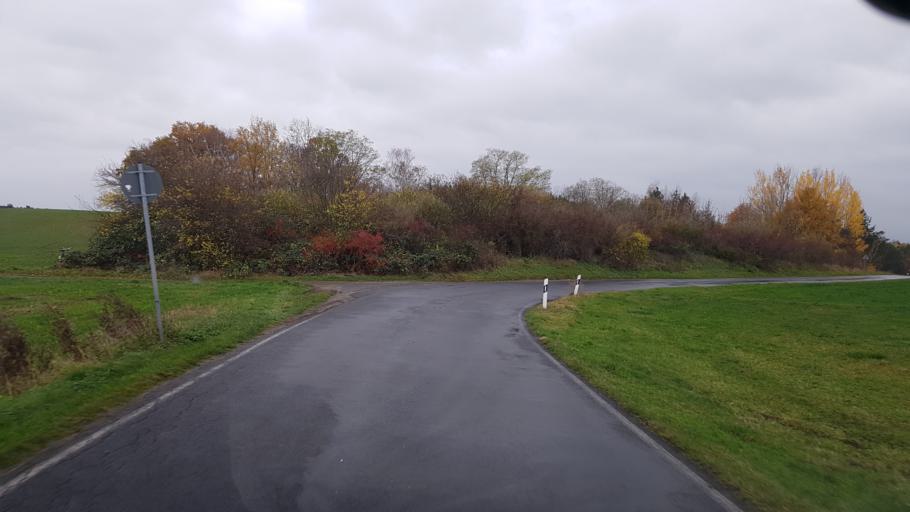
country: DE
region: Brandenburg
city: Ortrand
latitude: 51.3640
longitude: 13.7661
